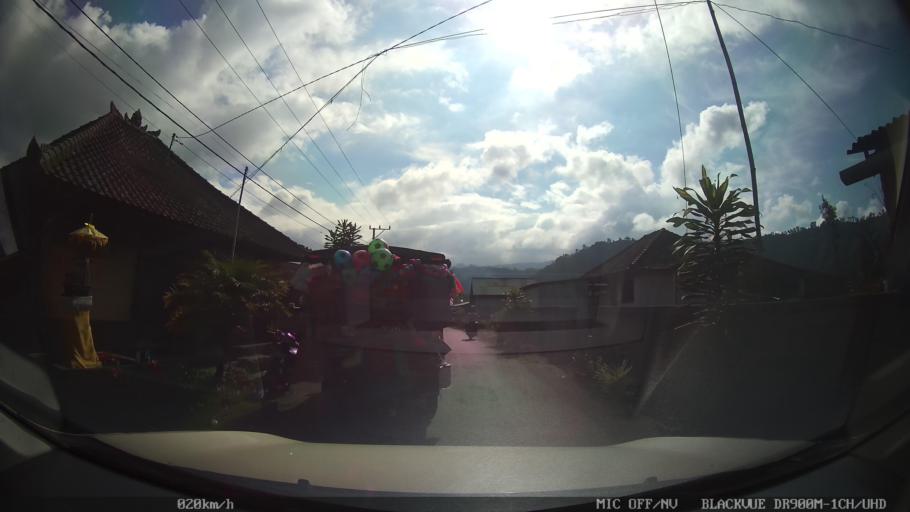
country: ID
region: Bali
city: Banjar Trunyan
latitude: -8.2165
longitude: 115.3866
